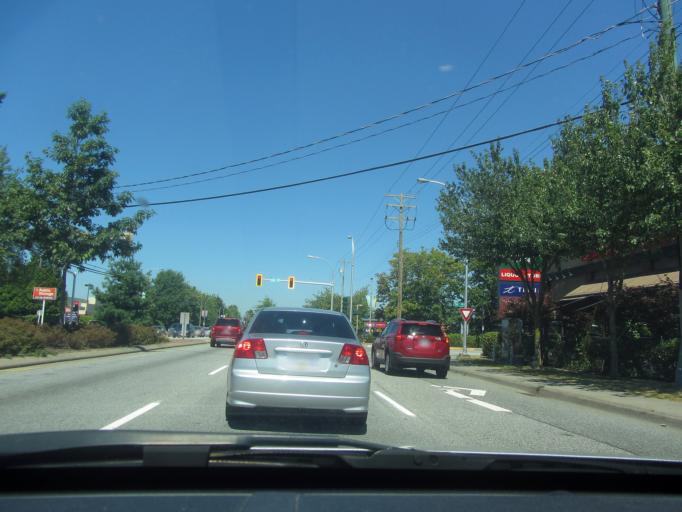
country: CA
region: British Columbia
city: Surrey
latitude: 49.1367
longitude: -122.8455
